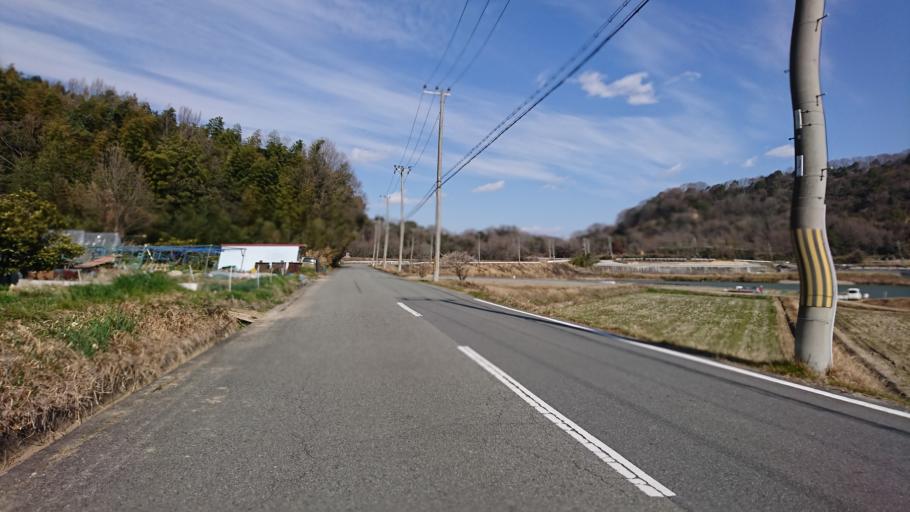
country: JP
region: Hyogo
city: Kakogawacho-honmachi
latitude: 34.8285
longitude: 134.8186
